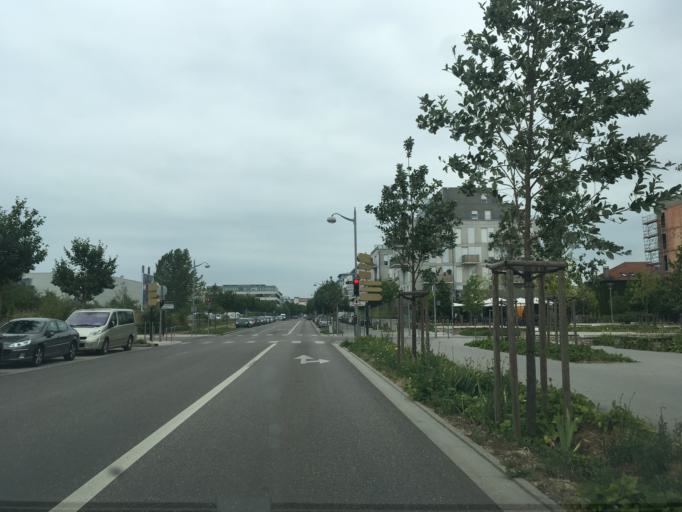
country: FR
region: Lorraine
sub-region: Departement de Meurthe-et-Moselle
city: Nancy
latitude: 48.6908
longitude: 6.1992
